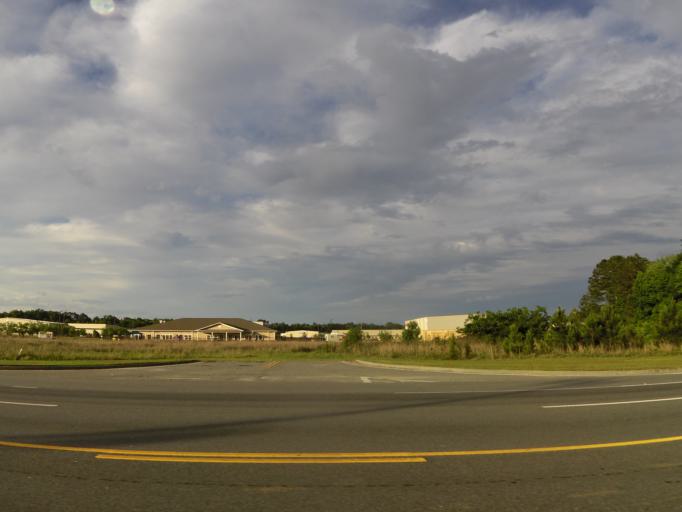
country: US
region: Georgia
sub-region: Chatham County
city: Pooler
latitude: 32.1025
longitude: -81.2244
